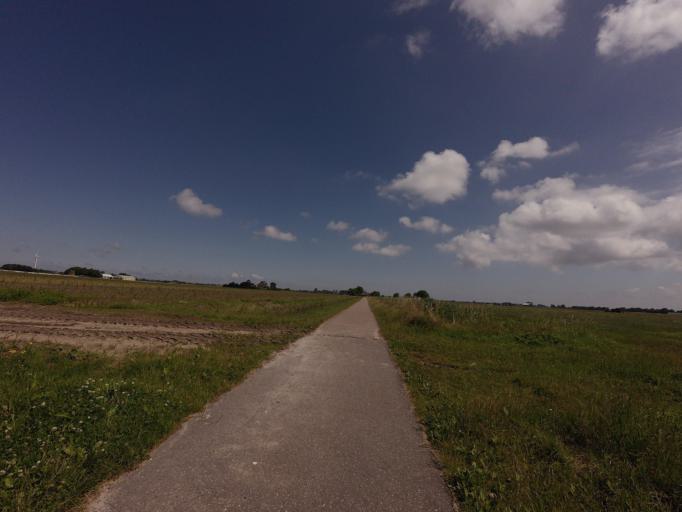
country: NL
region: North Holland
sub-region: Gemeente Schagen
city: Schagen
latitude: 52.8671
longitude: 4.8353
